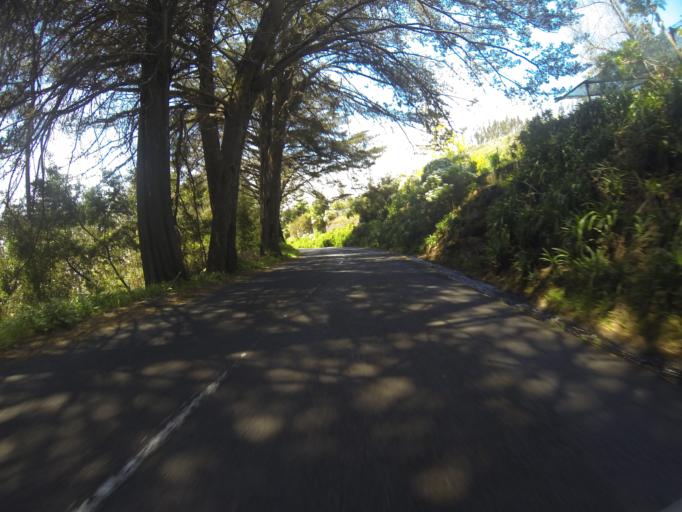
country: PT
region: Madeira
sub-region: Funchal
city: Nossa Senhora do Monte
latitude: 32.6944
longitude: -16.9022
